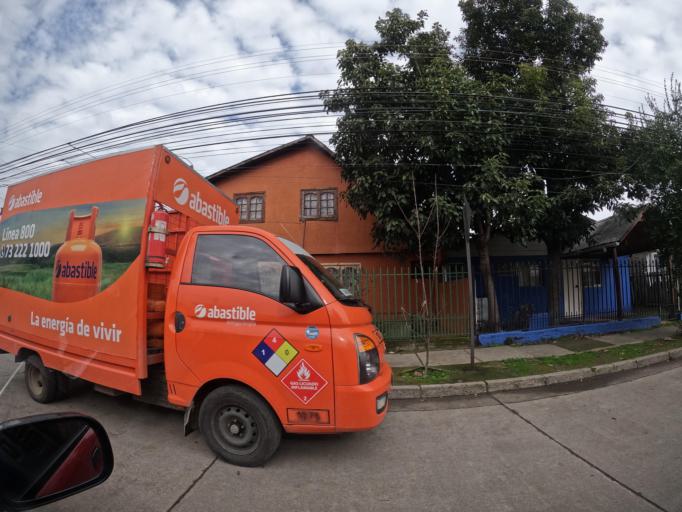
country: CL
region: Maule
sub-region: Provincia de Linares
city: Linares
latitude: -35.8528
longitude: -71.6061
